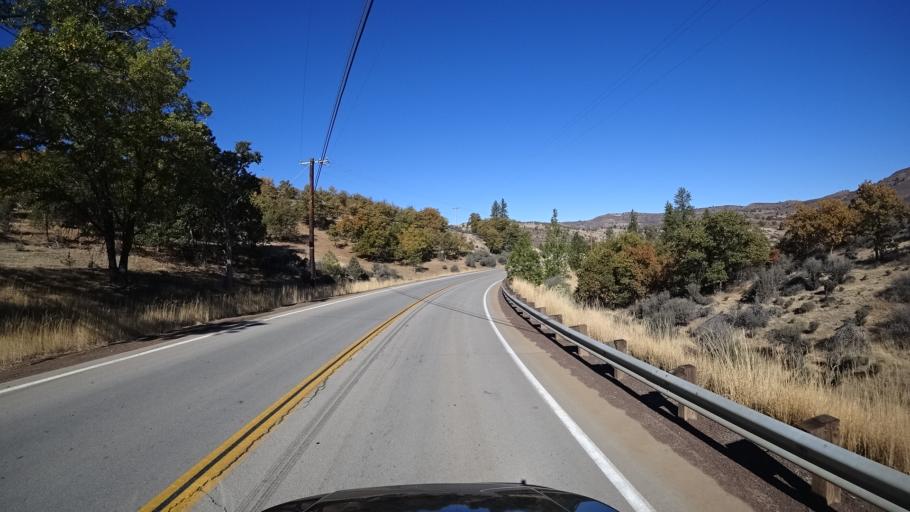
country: US
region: California
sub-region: Siskiyou County
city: Montague
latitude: 41.8950
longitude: -122.5063
